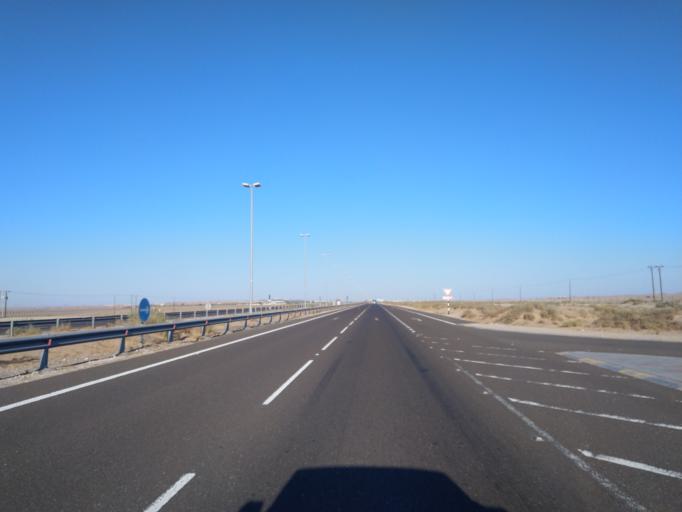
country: OM
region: Al Buraimi
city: Al Buraymi
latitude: 24.4978
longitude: 55.4322
